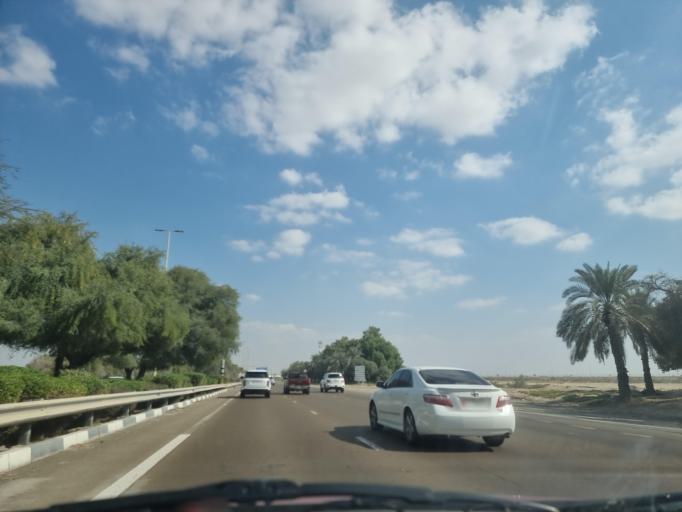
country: AE
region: Abu Dhabi
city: Abu Dhabi
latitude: 24.4098
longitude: 54.6580
